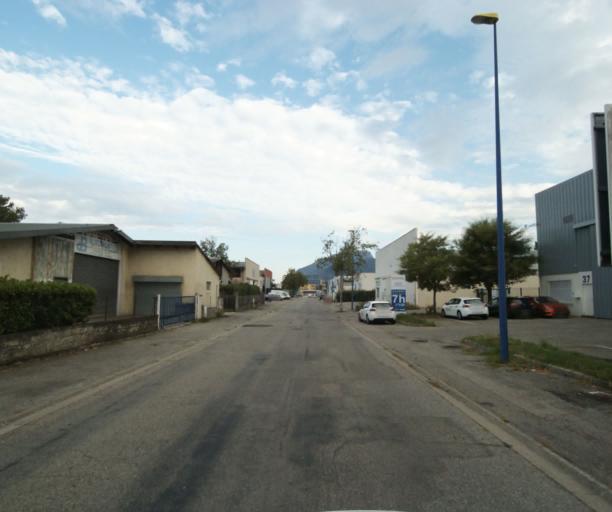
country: FR
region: Rhone-Alpes
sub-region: Departement de l'Isere
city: Poisat
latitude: 45.1620
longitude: 5.7614
